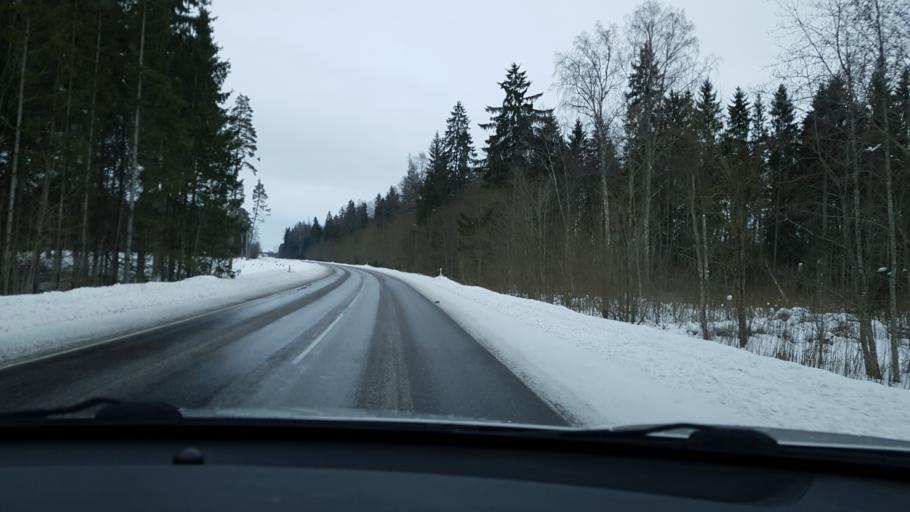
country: EE
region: Jaervamaa
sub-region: Jaerva-Jaani vald
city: Jarva-Jaani
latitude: 59.0981
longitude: 25.8190
